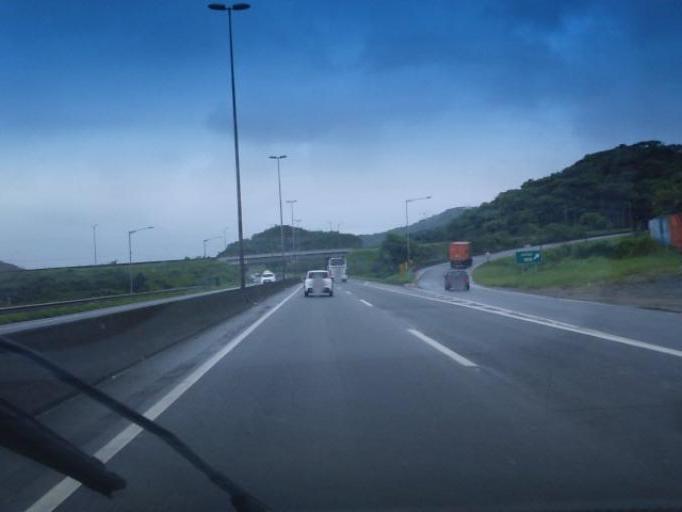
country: BR
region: Santa Catarina
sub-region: Penha
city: Penha
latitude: -26.8079
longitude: -48.6813
